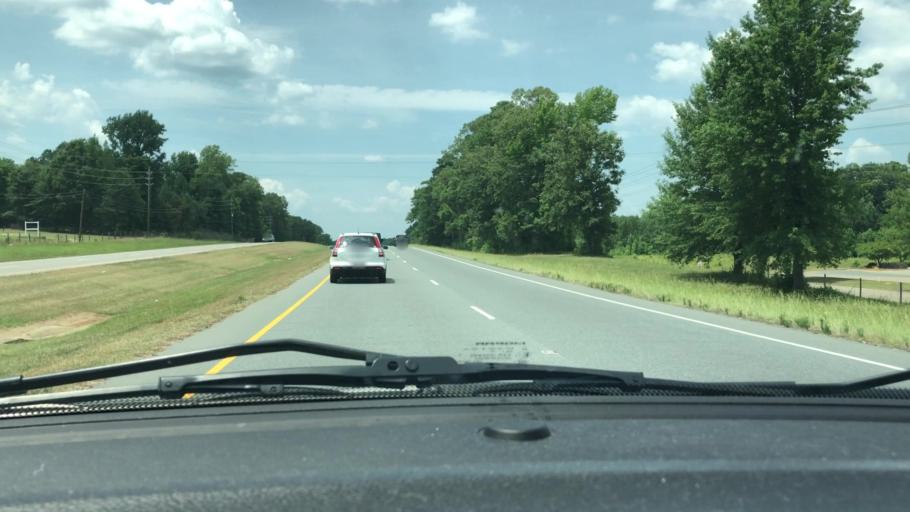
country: US
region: North Carolina
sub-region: Lee County
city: Sanford
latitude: 35.5049
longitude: -79.2075
